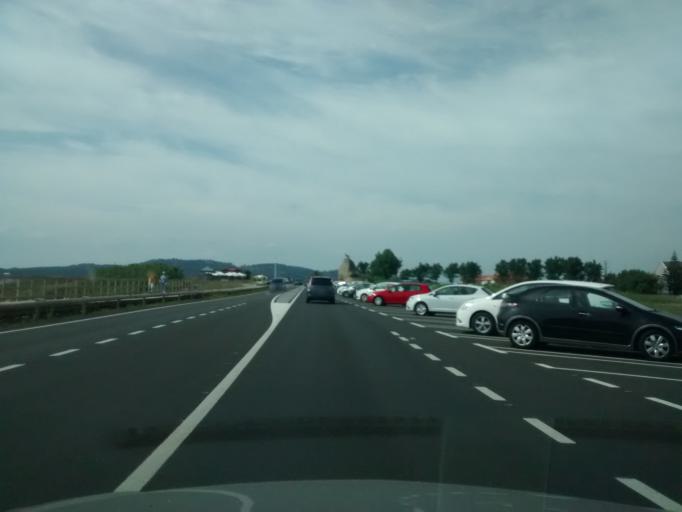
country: ES
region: Galicia
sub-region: Provincia de Pontevedra
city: O Grove
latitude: 42.4349
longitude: -8.8704
